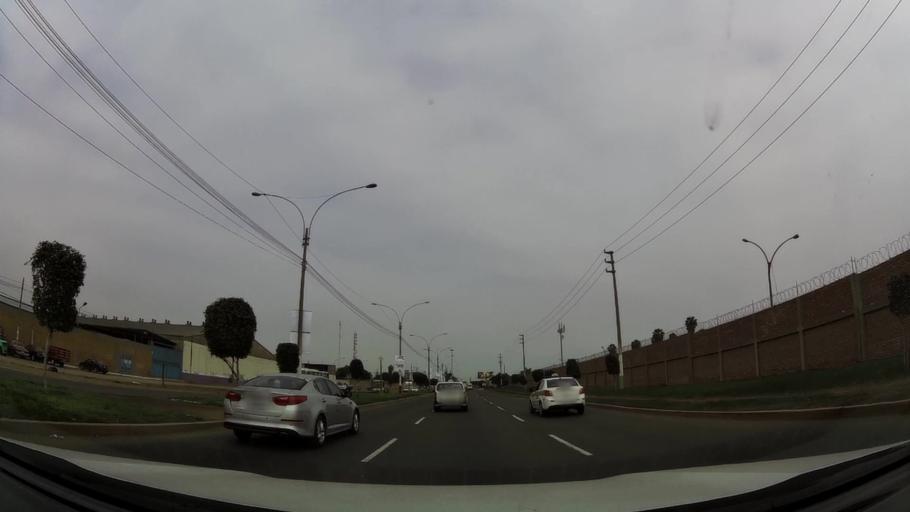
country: PE
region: Callao
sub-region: Callao
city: Callao
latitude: -12.0081
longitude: -77.1130
